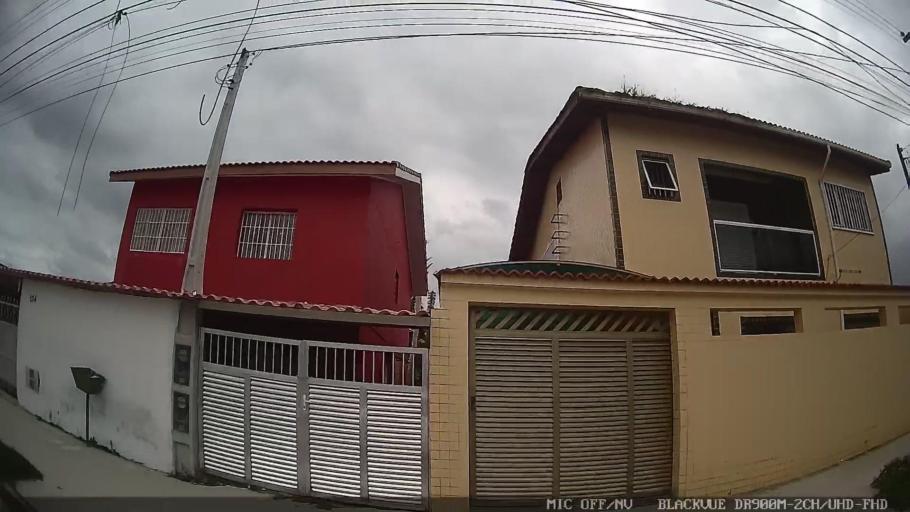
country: BR
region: Sao Paulo
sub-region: Guaruja
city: Guaruja
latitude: -23.9939
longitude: -46.2878
